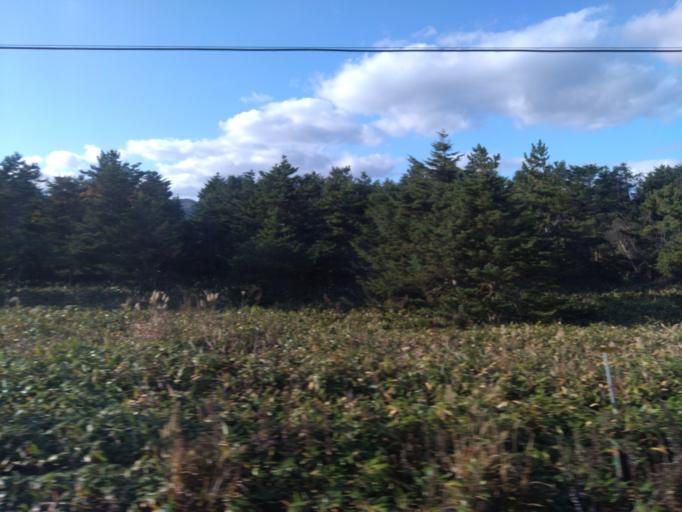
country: JP
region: Hokkaido
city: Niseko Town
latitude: 42.5752
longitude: 140.4482
